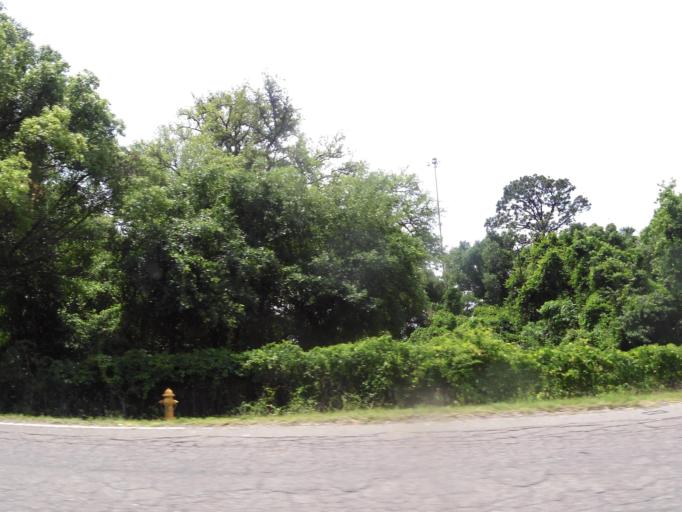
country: US
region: Florida
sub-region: Duval County
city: Jacksonville
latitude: 30.4132
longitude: -81.5628
